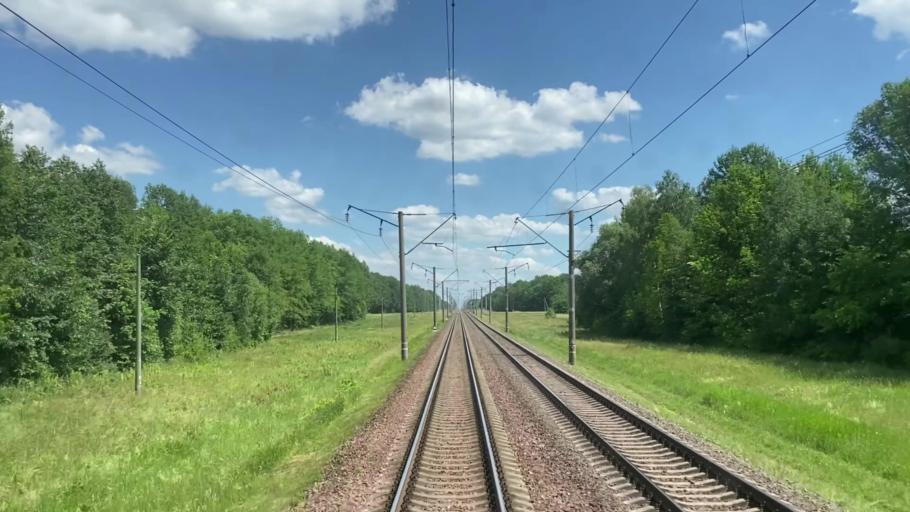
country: BY
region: Brest
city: Pruzhany
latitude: 52.5057
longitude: 24.6633
